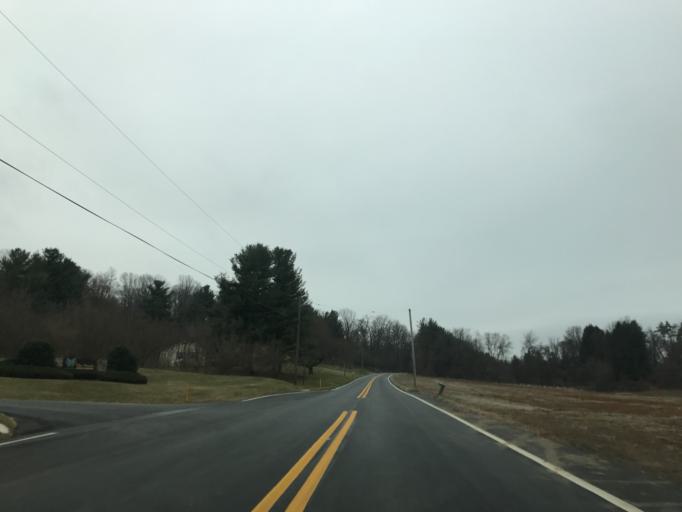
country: US
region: Maryland
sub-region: Carroll County
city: Westminster
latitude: 39.5535
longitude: -77.0338
